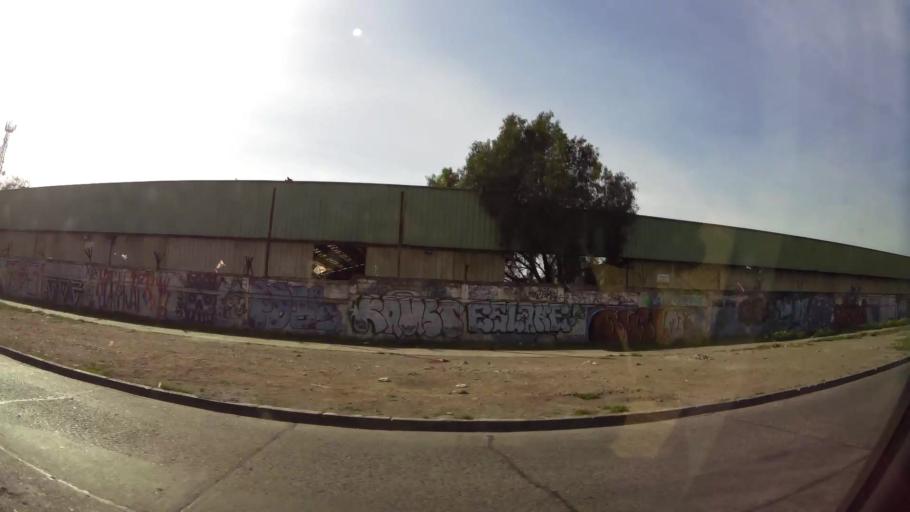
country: CL
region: Santiago Metropolitan
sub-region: Provincia de Santiago
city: La Pintana
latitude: -33.5277
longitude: -70.6260
